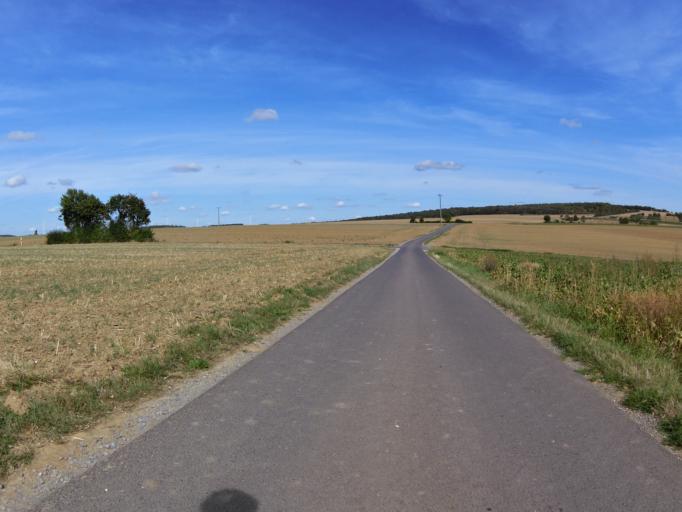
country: DE
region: Bavaria
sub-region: Regierungsbezirk Unterfranken
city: Rimpar
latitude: 49.8552
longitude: 9.9365
